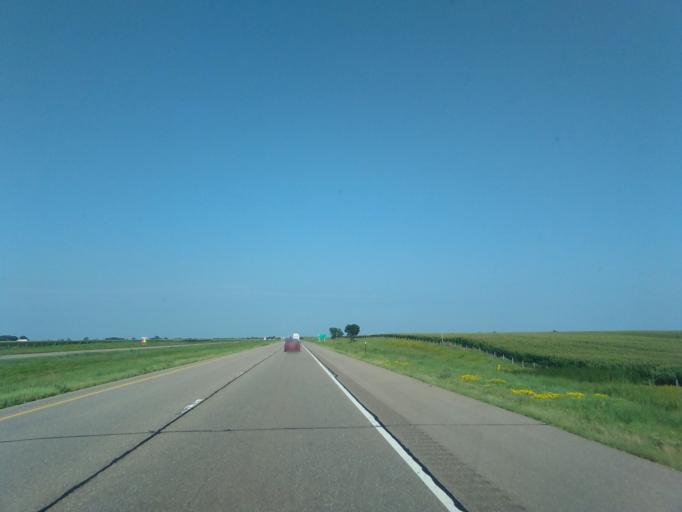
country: US
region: Nebraska
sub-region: Hamilton County
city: Aurora
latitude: 40.8221
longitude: -98.1373
